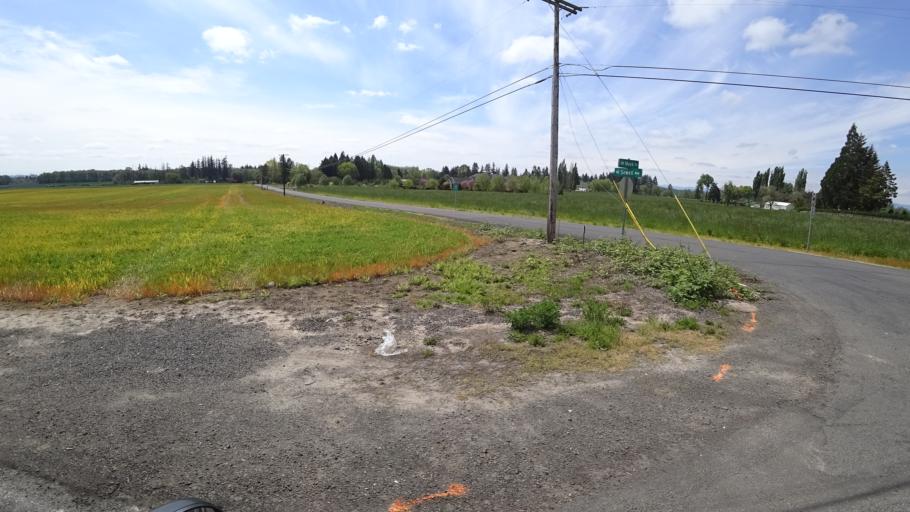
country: US
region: Oregon
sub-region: Washington County
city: North Plains
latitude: 45.5664
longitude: -122.9497
